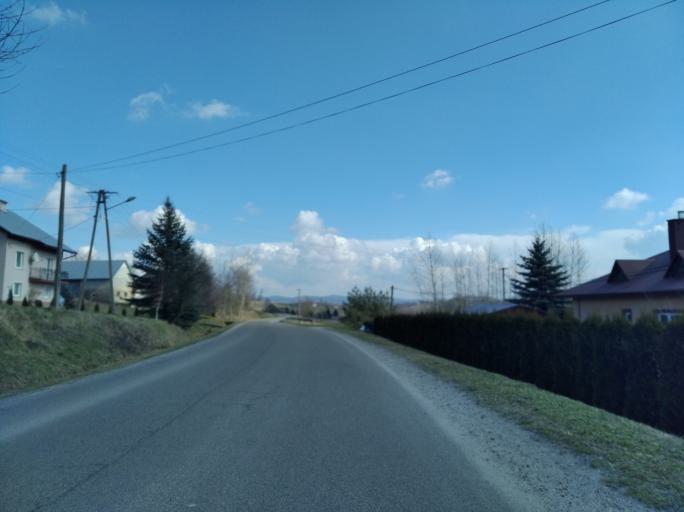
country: PL
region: Subcarpathian Voivodeship
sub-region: Powiat strzyzowski
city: Frysztak
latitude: 49.8473
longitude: 21.5506
